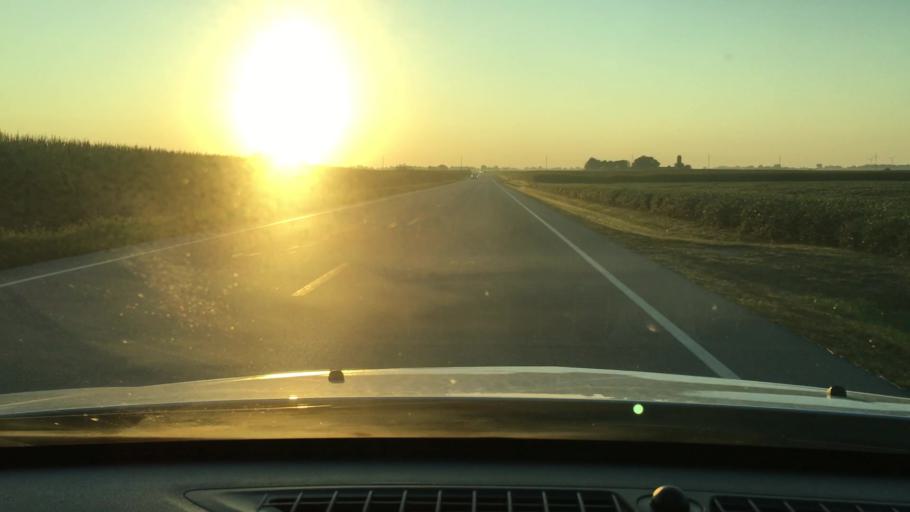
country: US
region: Illinois
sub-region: DeKalb County
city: Malta
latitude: 41.8487
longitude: -88.8399
